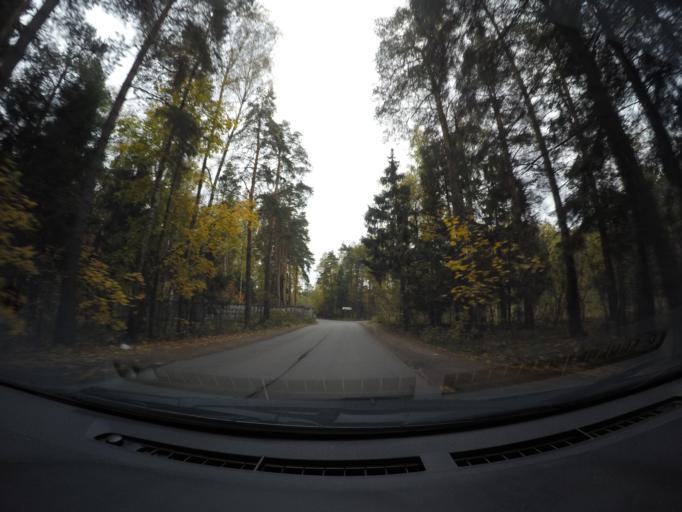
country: RU
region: Moskovskaya
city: Vishnyakovskiye Dachi
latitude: 55.8104
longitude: 38.1096
